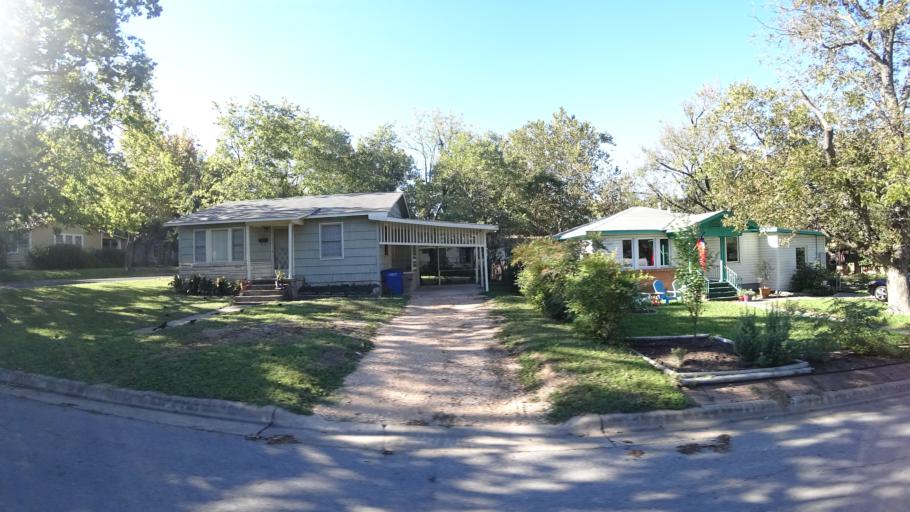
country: US
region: Texas
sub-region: Travis County
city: Austin
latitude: 30.3134
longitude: -97.7239
